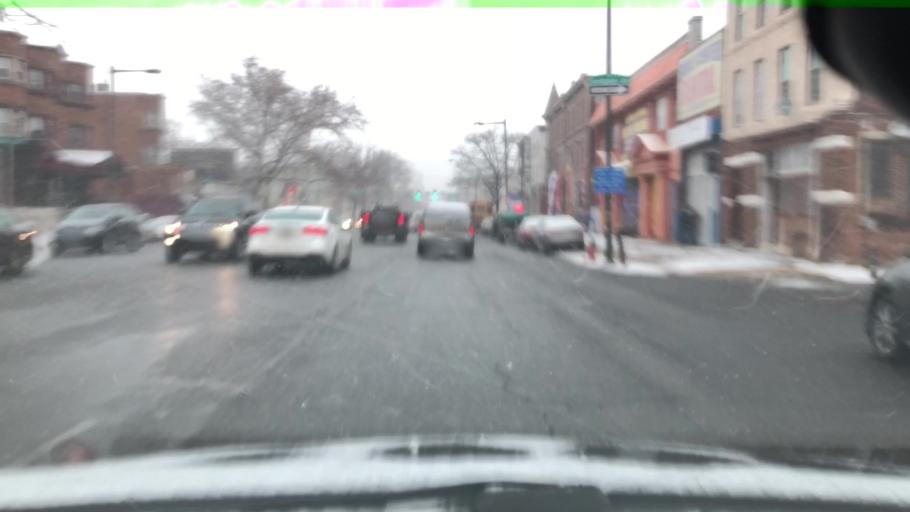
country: US
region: Pennsylvania
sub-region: Philadelphia County
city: Philadelphia
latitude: 39.9986
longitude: -75.1535
